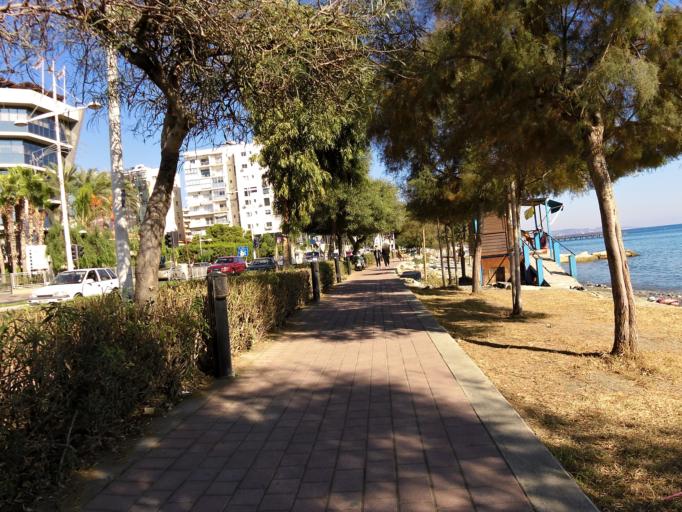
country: CY
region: Limassol
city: Limassol
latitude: 34.6834
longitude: 33.0577
